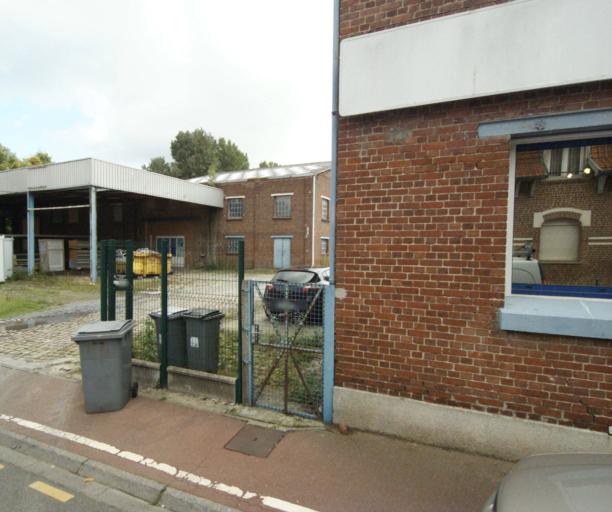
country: FR
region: Nord-Pas-de-Calais
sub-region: Departement du Nord
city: Herlies
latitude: 50.5804
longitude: 2.8527
